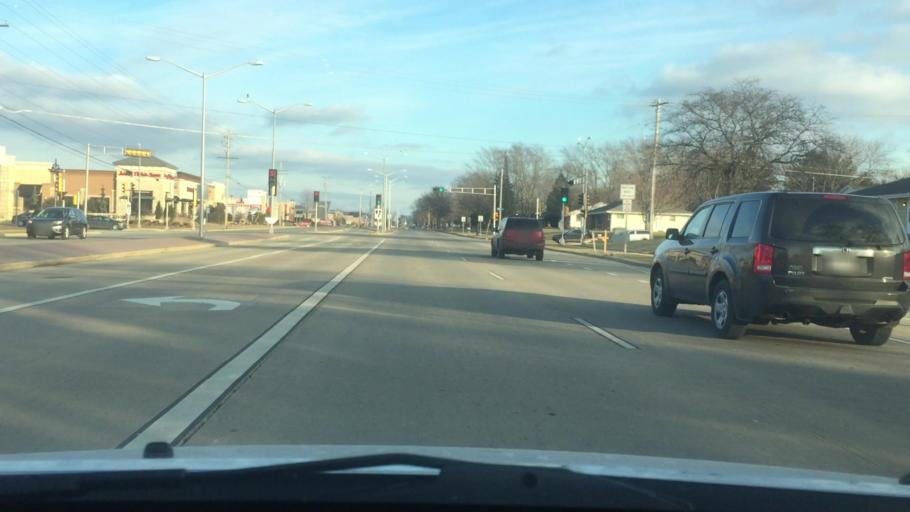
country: US
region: Wisconsin
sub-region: Waukesha County
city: Waukesha
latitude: 42.9883
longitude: -88.2582
